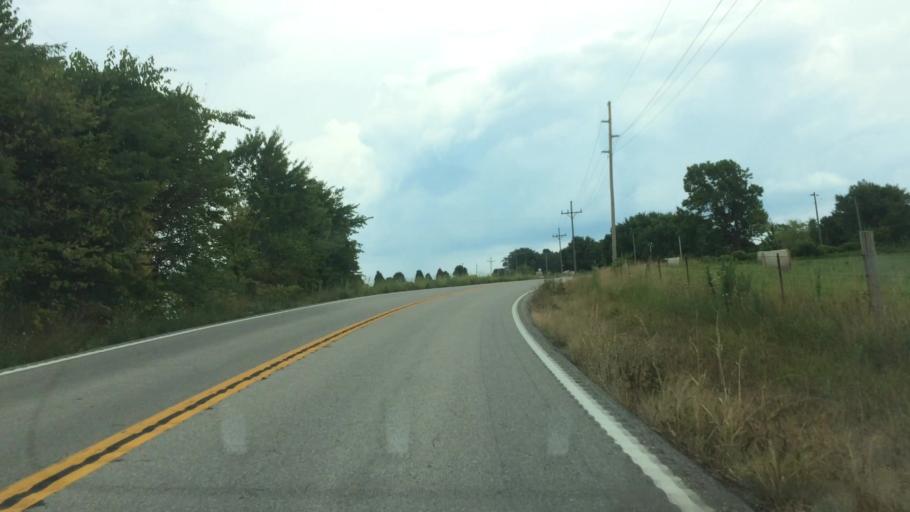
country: US
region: Missouri
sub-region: Greene County
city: Strafford
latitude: 37.2429
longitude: -93.1361
